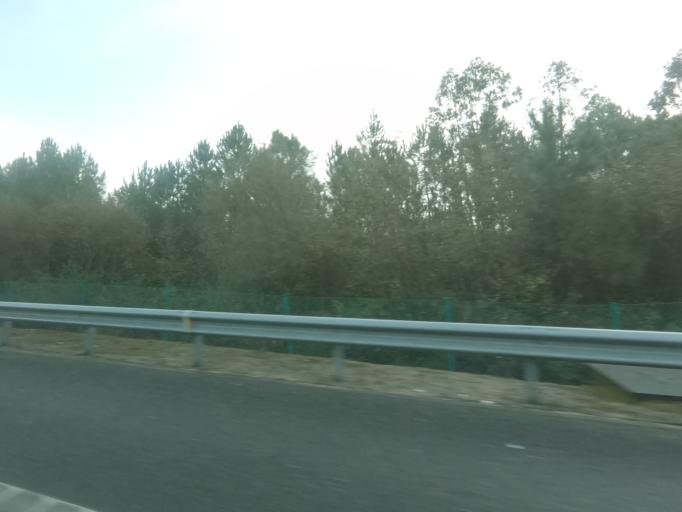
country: ES
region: Galicia
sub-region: Provincia de Pontevedra
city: Tui
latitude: 42.0716
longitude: -8.6395
